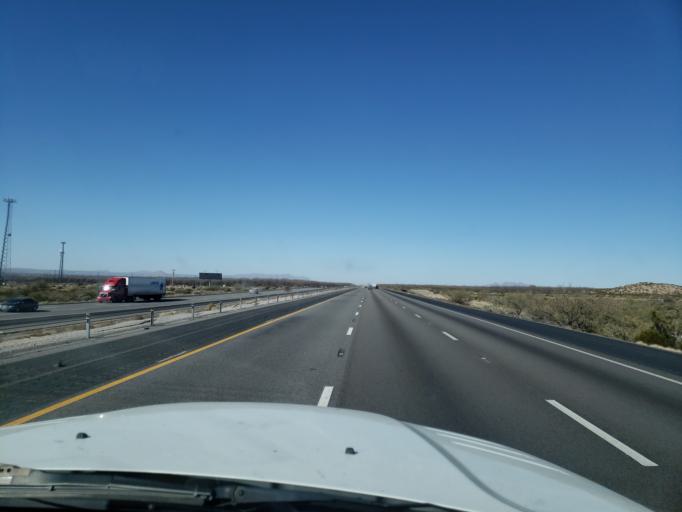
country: US
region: New Mexico
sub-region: Dona Ana County
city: Mesquite
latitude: 32.2197
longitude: -106.7025
